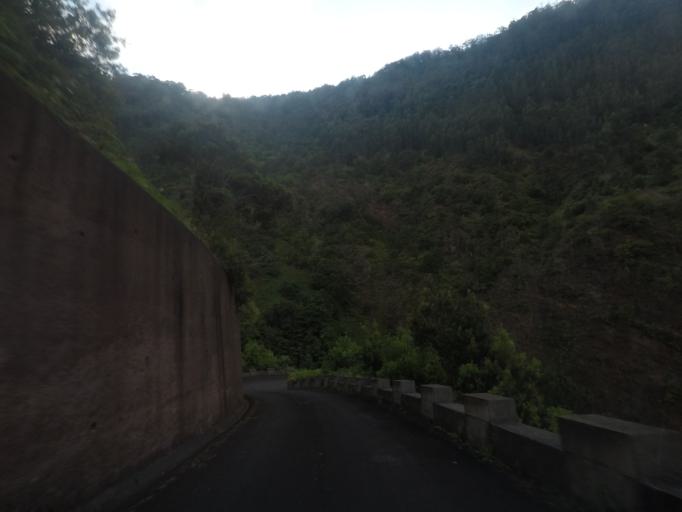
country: PT
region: Madeira
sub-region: Porto Moniz
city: Porto Moniz
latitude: 32.8469
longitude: -17.1636
